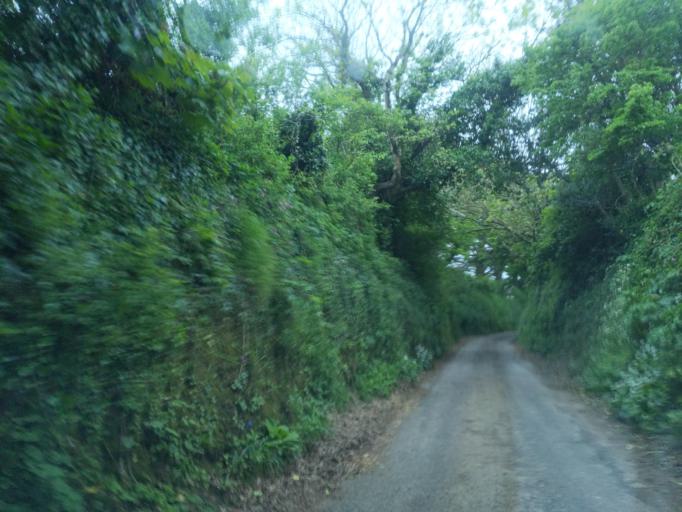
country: GB
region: England
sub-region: Borough of Torbay
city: Brixham
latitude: 50.3641
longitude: -3.5301
